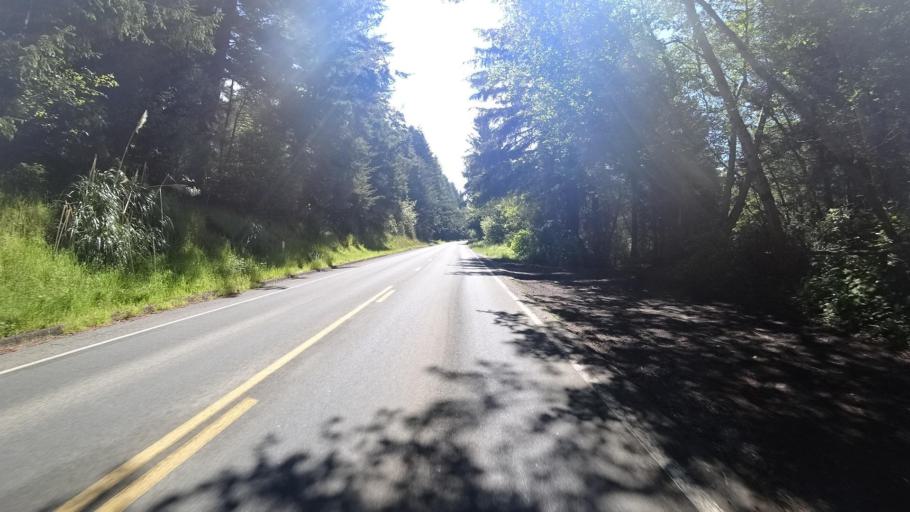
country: US
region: California
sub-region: Humboldt County
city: McKinleyville
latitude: 40.9560
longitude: -124.0871
